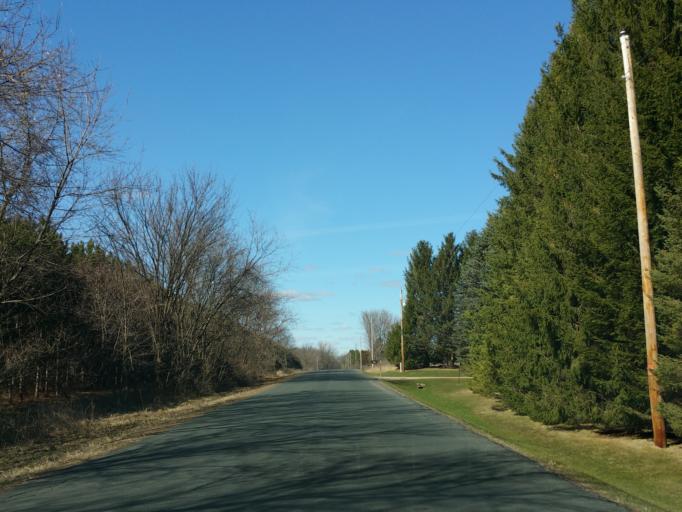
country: US
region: Minnesota
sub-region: Washington County
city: Stillwater
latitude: 45.0794
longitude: -92.7714
